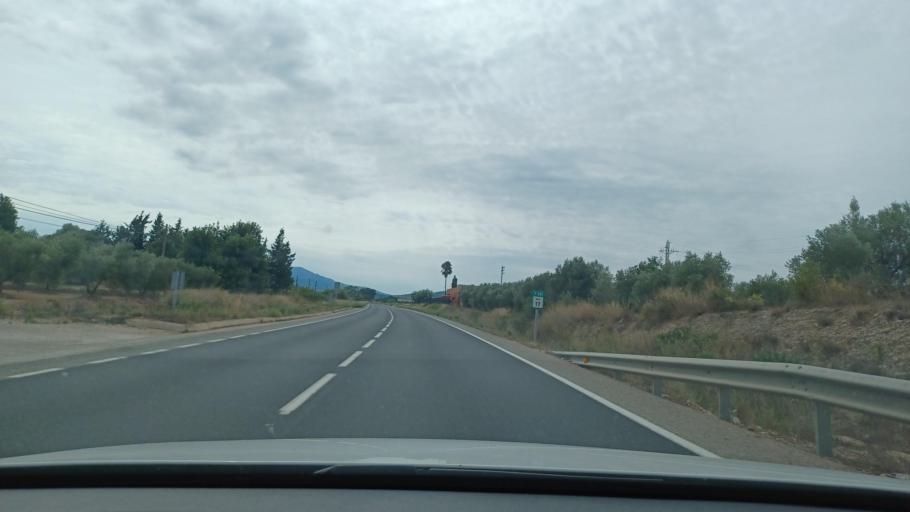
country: ES
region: Catalonia
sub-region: Provincia de Tarragona
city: Santa Barbara
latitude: 40.7345
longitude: 0.5031
